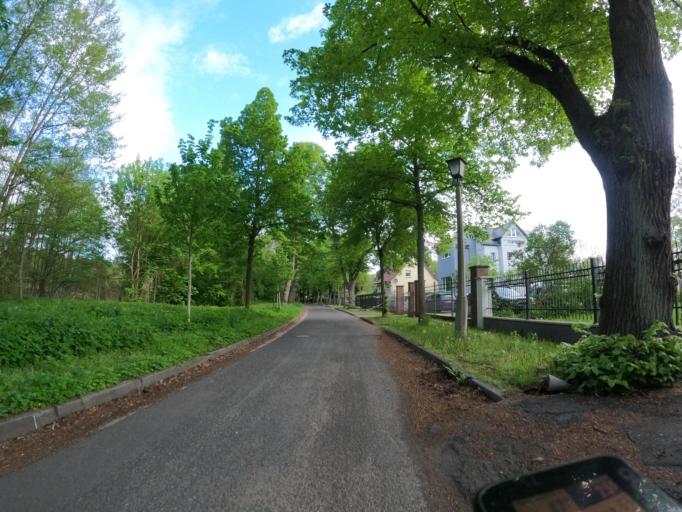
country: DE
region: Brandenburg
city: Konigs Wusterhausen
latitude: 52.2978
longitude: 13.6469
